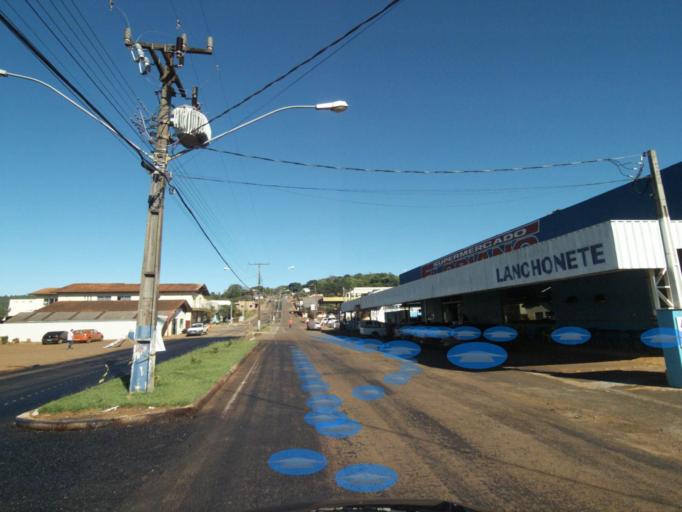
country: BR
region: Parana
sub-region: Coronel Vivida
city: Coronel Vivida
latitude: -26.1434
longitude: -52.3820
